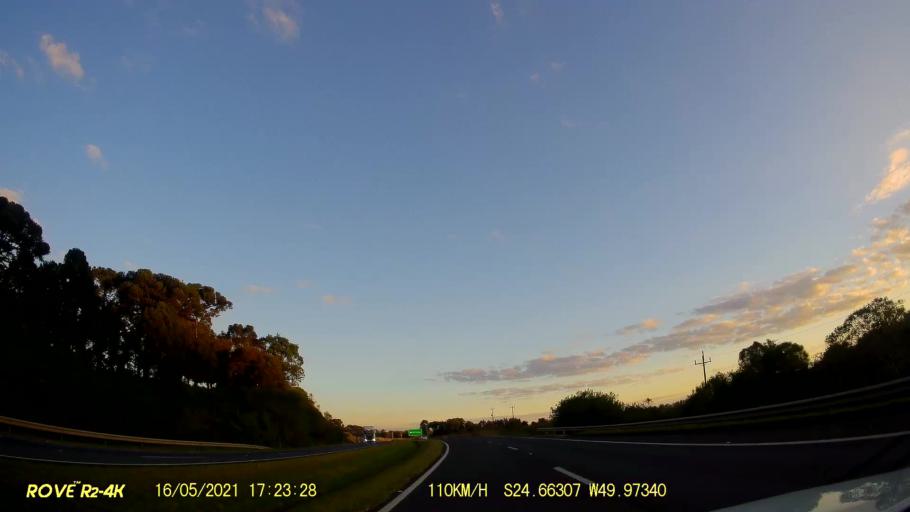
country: BR
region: Parana
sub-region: Castro
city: Castro
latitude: -24.6634
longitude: -49.9734
